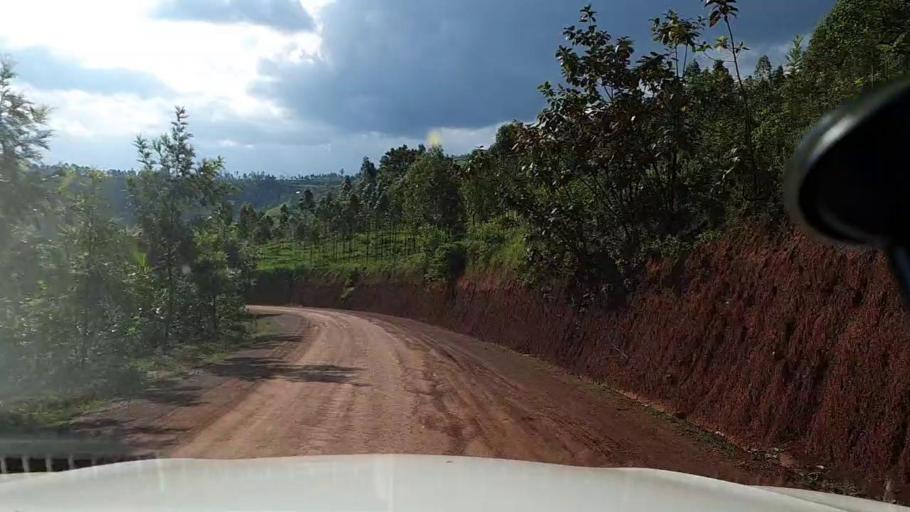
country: RW
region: Kigali
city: Kigali
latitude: -1.8447
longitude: 29.8582
